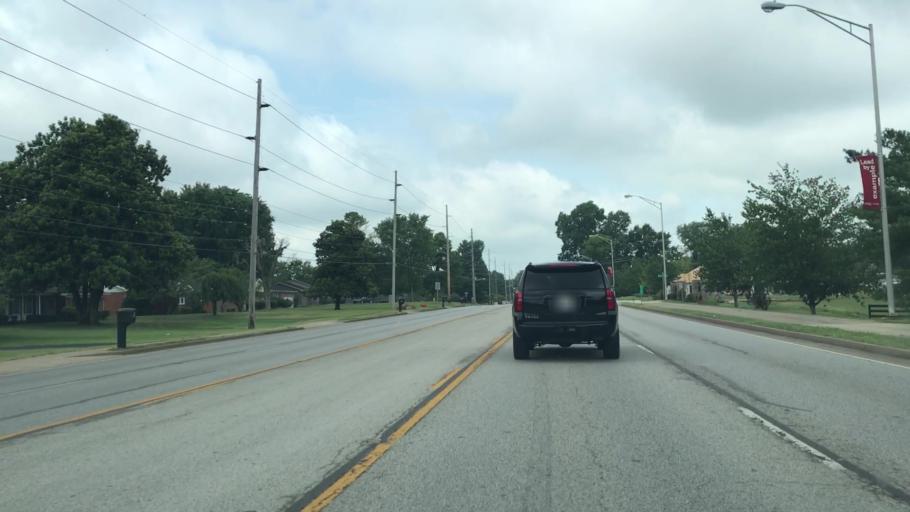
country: US
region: Kentucky
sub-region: Warren County
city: Bowling Green
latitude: 36.9898
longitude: -86.4132
